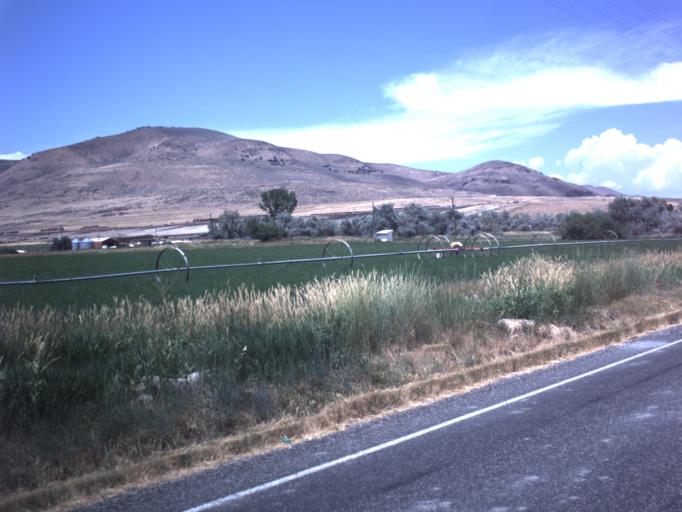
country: US
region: Utah
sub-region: Box Elder County
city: Tremonton
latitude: 41.6564
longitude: -112.2960
